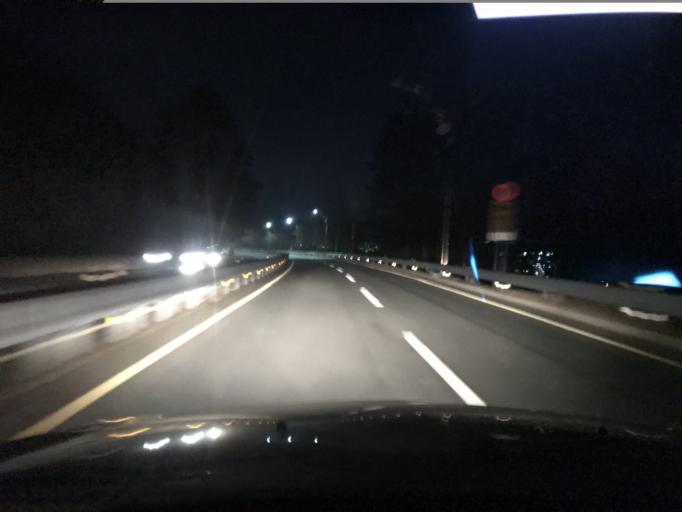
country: KR
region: Daegu
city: Hwawon
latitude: 35.7431
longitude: 128.4785
